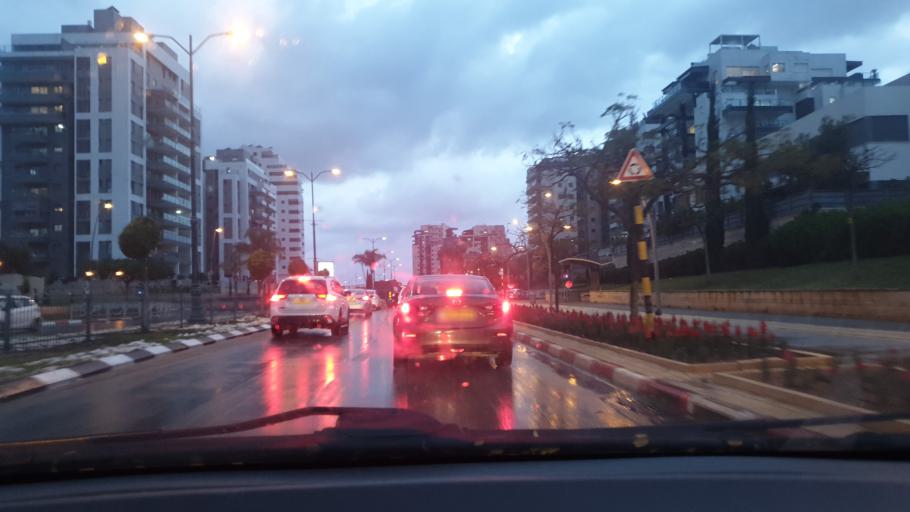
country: IL
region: Central District
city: Rishon LeZiyyon
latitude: 31.9812
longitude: 34.8081
